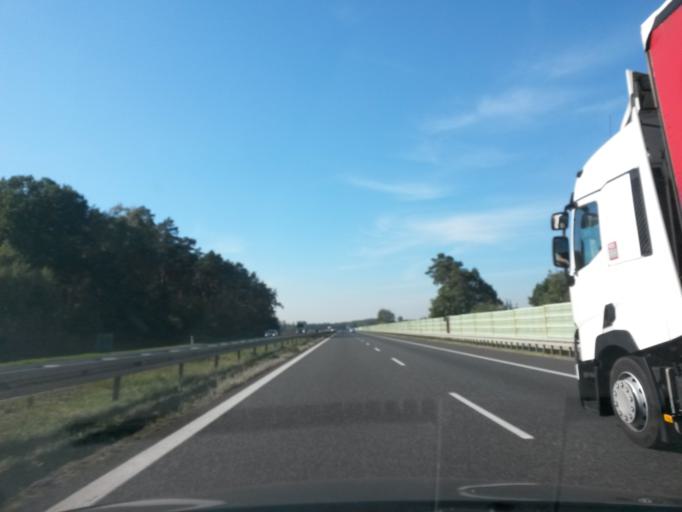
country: PL
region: Silesian Voivodeship
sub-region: Powiat gliwicki
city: Rudziniec
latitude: 50.3761
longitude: 18.4780
